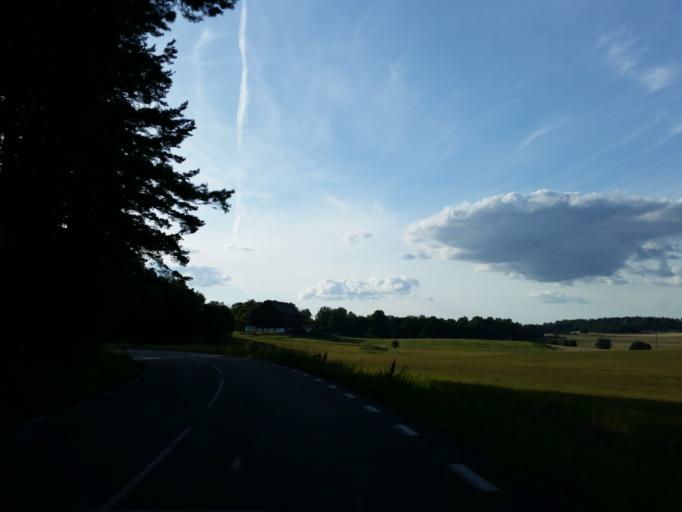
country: SE
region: Stockholm
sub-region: Sodertalje Kommun
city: Molnbo
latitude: 59.0128
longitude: 17.3736
